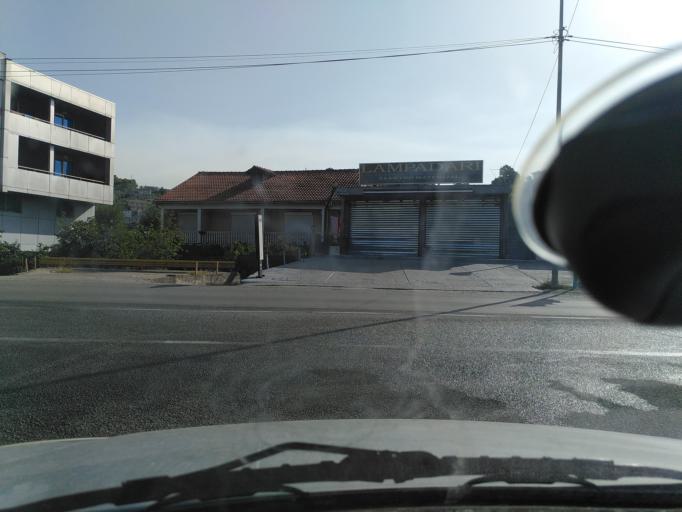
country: ME
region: Ulcinj
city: Ulcinj
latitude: 41.9333
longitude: 19.2229
